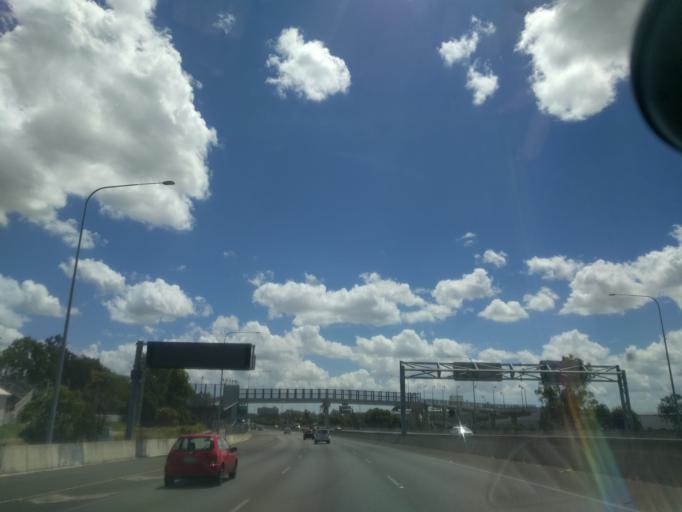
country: AU
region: Queensland
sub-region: Brisbane
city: Wacol
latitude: -27.6030
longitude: 152.9191
